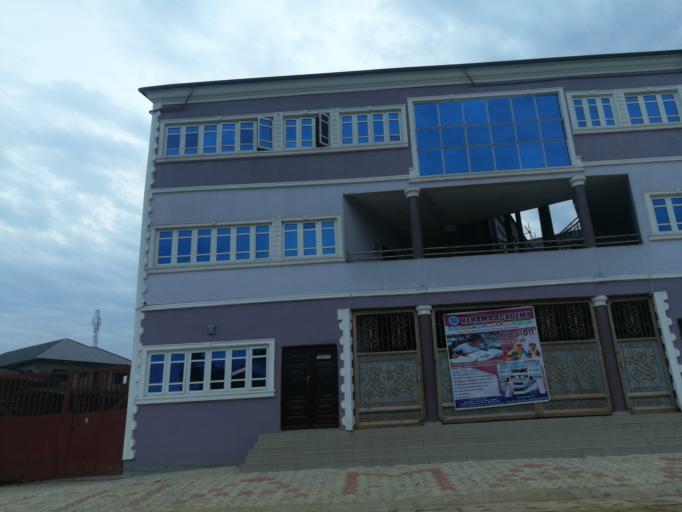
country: NG
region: Rivers
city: Port Harcourt
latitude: 4.7930
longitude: 6.9566
